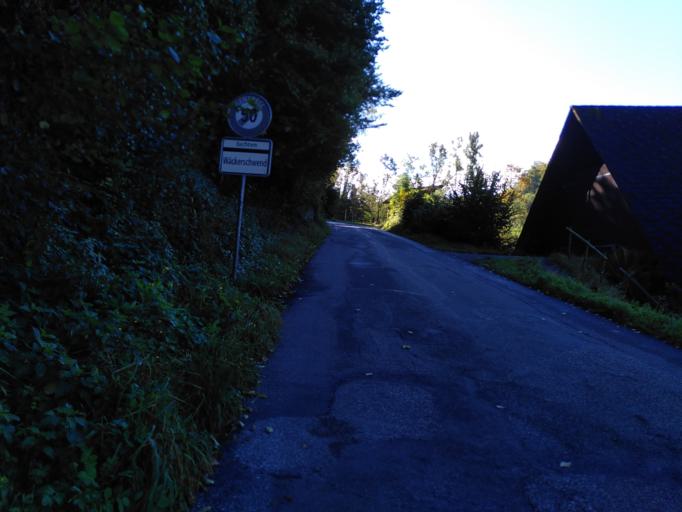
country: CH
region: Bern
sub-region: Oberaargau
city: Seeberg
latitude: 47.1391
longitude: 7.7029
